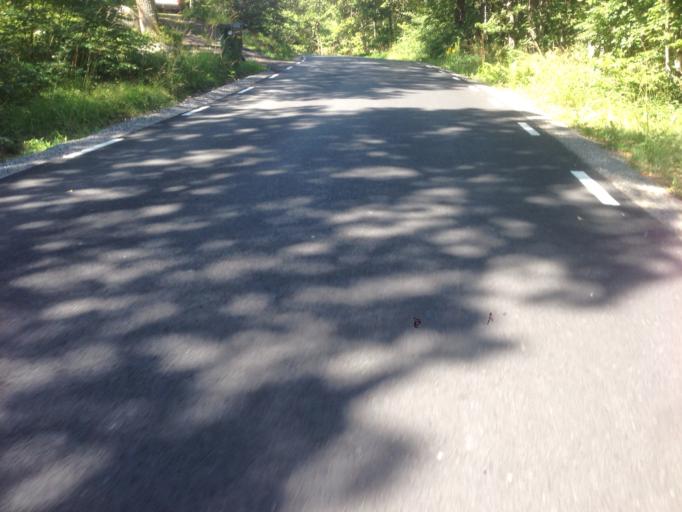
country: SE
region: Stockholm
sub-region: Vaxholms Kommun
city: Vaxholm
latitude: 59.3828
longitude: 18.3711
